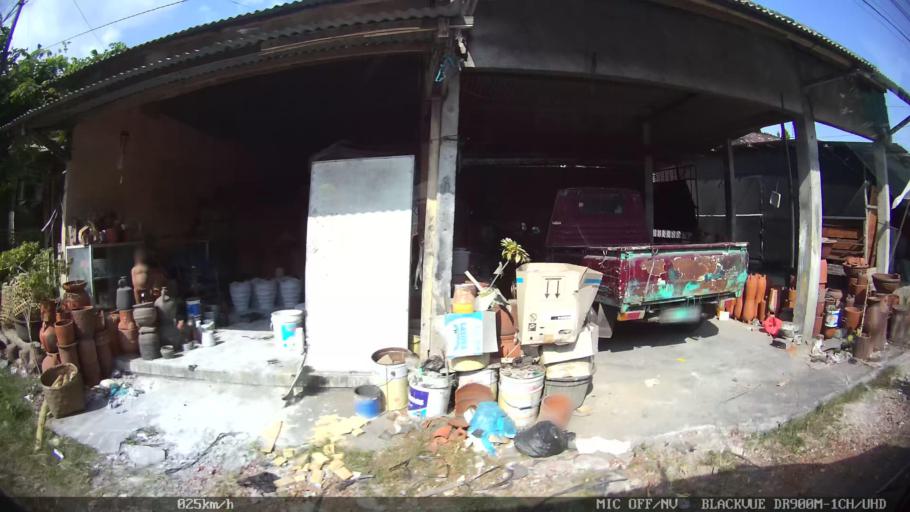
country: ID
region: Daerah Istimewa Yogyakarta
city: Kasihan
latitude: -7.8441
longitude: 110.3350
